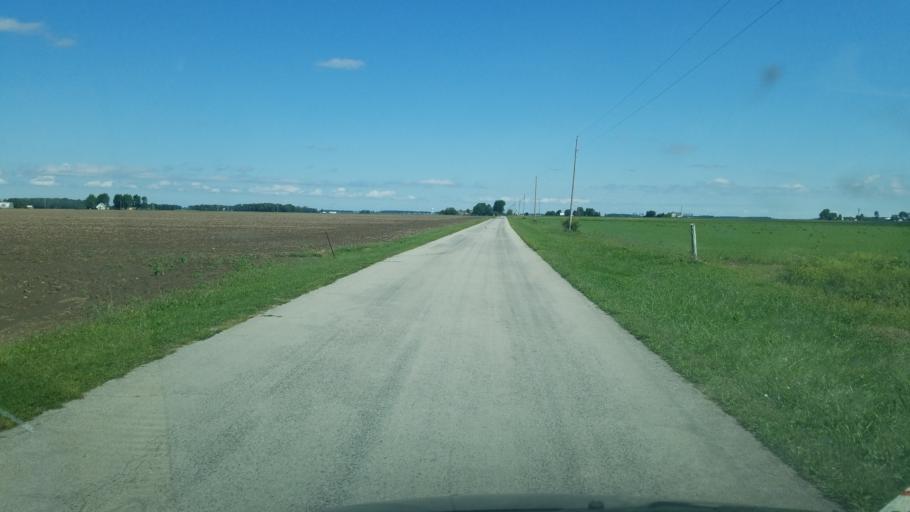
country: US
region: Ohio
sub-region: Hancock County
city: McComb
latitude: 41.1423
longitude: -83.7463
